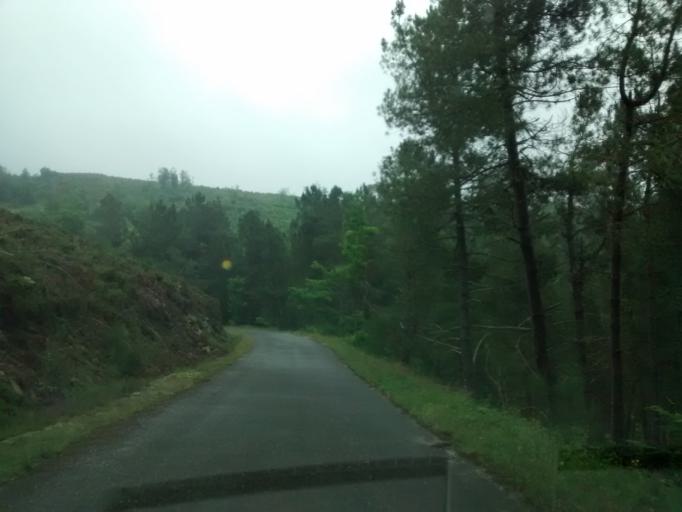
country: ES
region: Galicia
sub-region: Provincia de Ourense
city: Castro Caldelas
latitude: 42.4087
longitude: -7.3937
